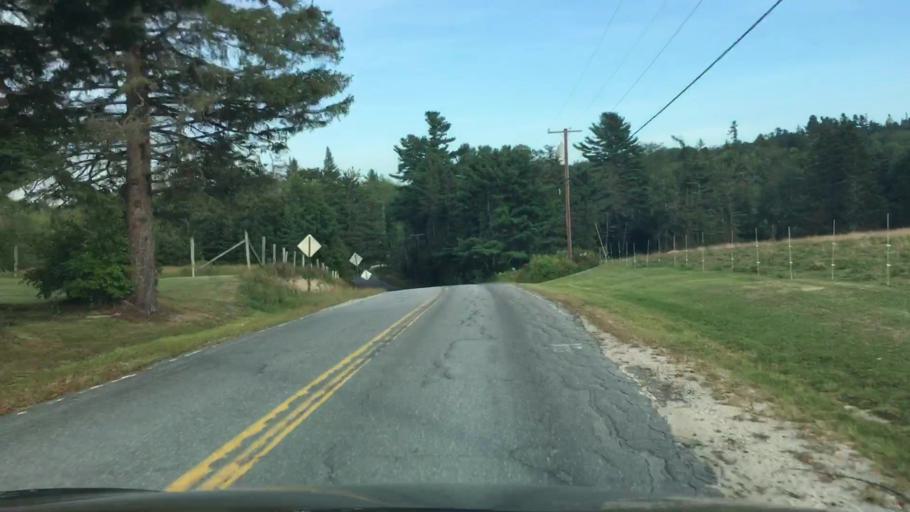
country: US
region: Maine
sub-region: Hancock County
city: Surry
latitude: 44.4940
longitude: -68.5184
